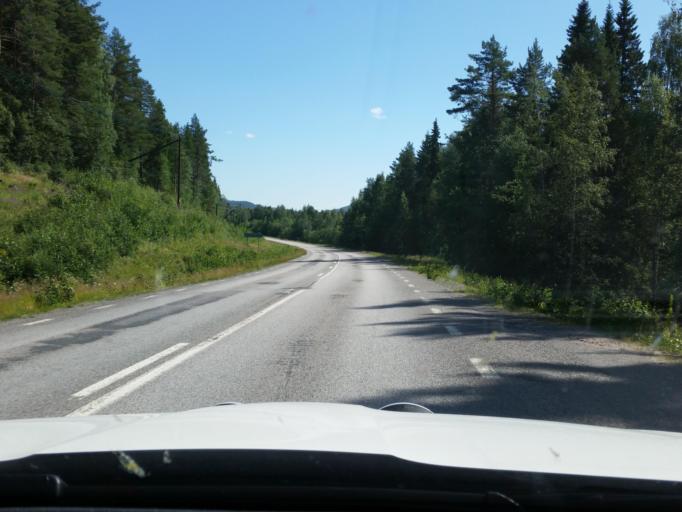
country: SE
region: Norrbotten
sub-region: Alvsbyns Kommun
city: AElvsbyn
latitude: 65.6800
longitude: 20.7455
